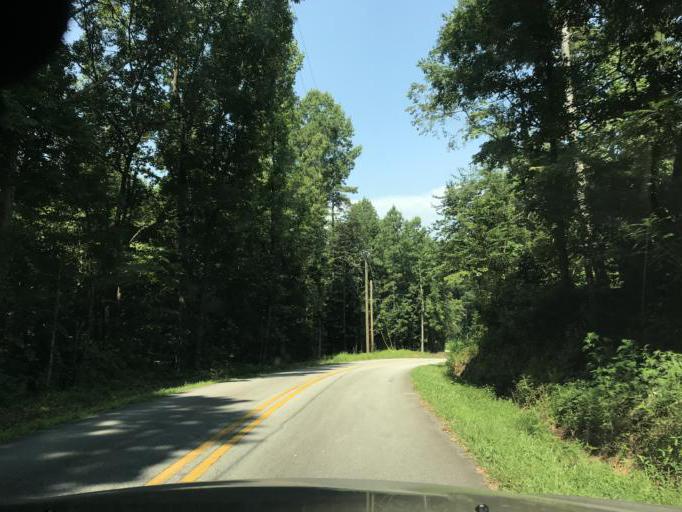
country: US
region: Georgia
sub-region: Dawson County
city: Dawsonville
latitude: 34.3330
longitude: -84.0627
